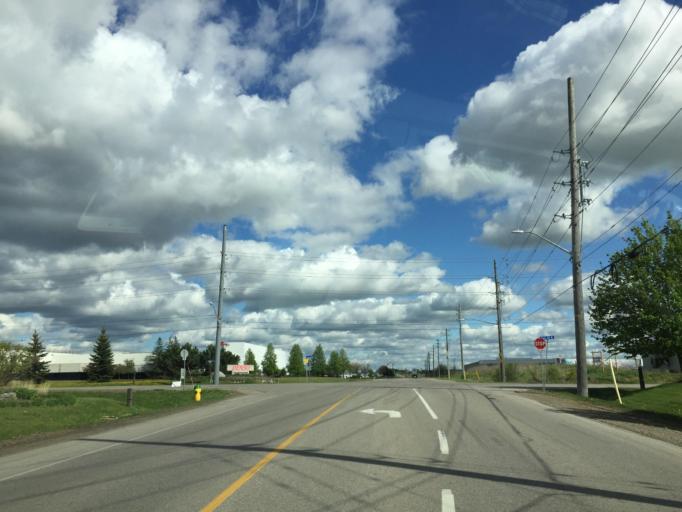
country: CA
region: Ontario
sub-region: Wellington County
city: Guelph
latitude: 43.4898
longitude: -80.2040
